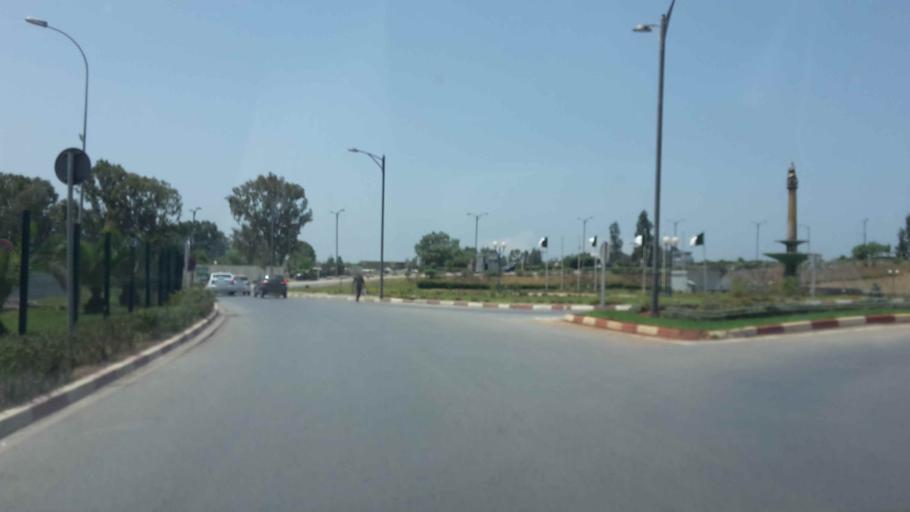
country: DZ
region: Alger
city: Dar el Beida
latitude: 36.7015
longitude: 3.2080
